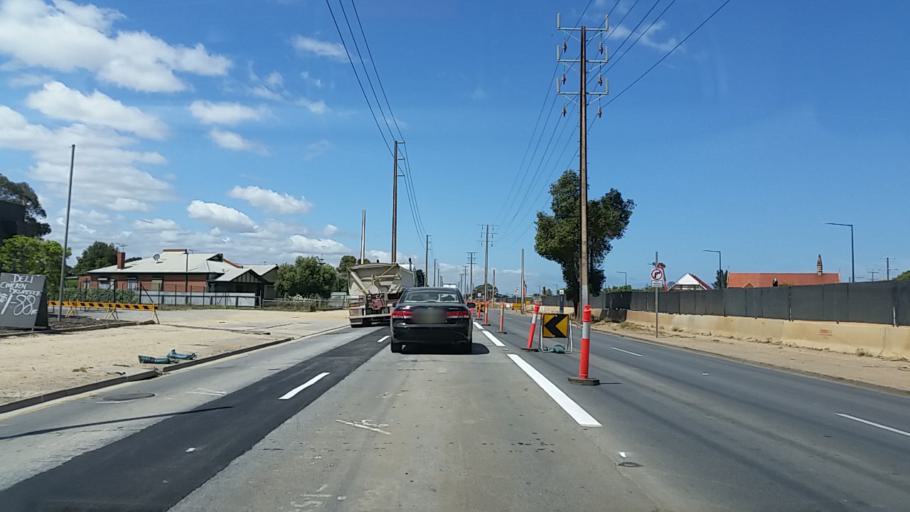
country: AU
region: South Australia
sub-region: Charles Sturt
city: Allenby Gardens
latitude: -34.8939
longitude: 138.5685
